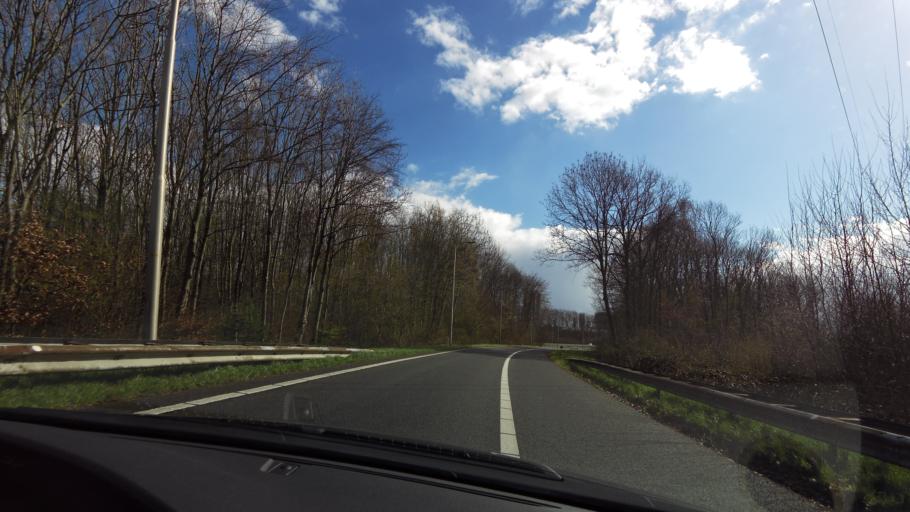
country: NL
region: Limburg
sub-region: Gemeente Stein
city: Stein
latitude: 50.9659
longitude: 5.7846
